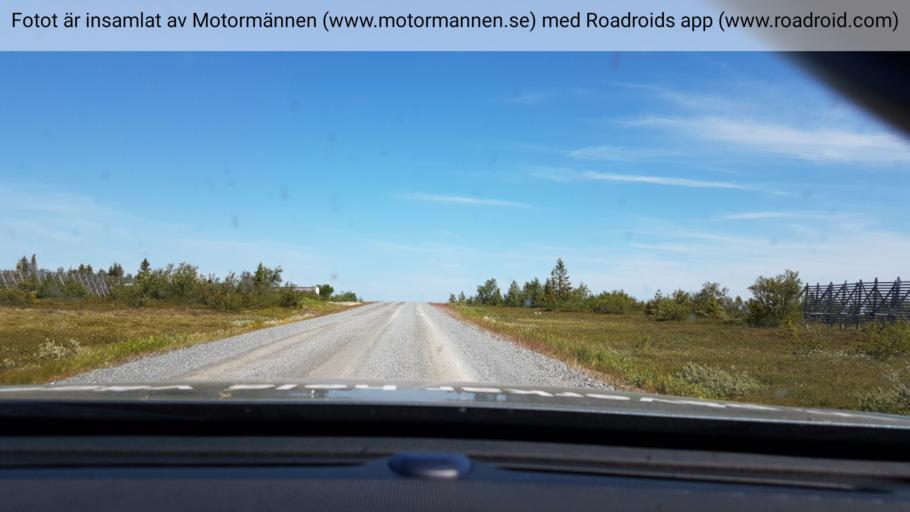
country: SE
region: Vaesterbotten
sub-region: Vilhelmina Kommun
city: Sjoberg
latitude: 64.7506
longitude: 15.8234
